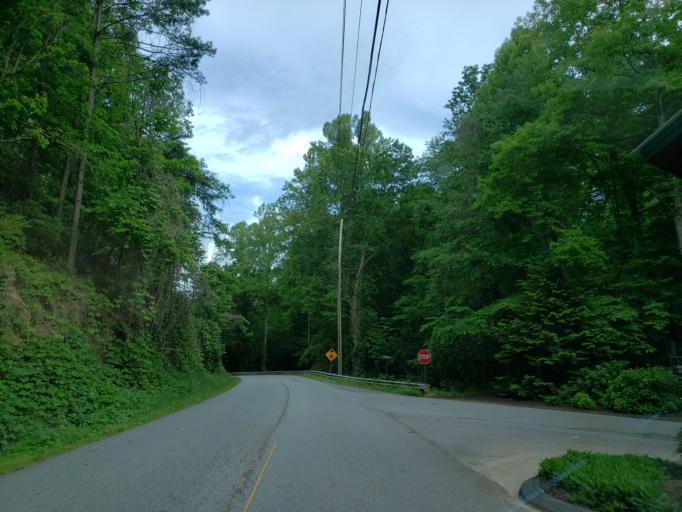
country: US
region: Georgia
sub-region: Fannin County
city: Blue Ridge
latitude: 34.8571
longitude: -84.3390
